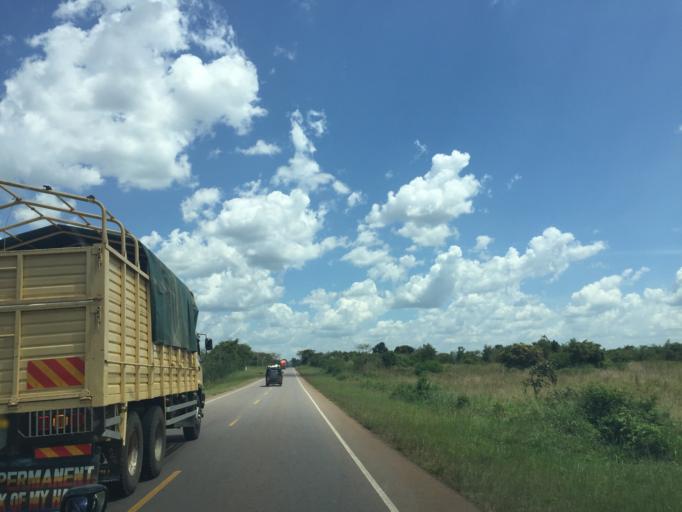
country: UG
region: Central Region
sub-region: Nakasongola District
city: Nakasongola
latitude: 1.3514
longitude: 32.3816
